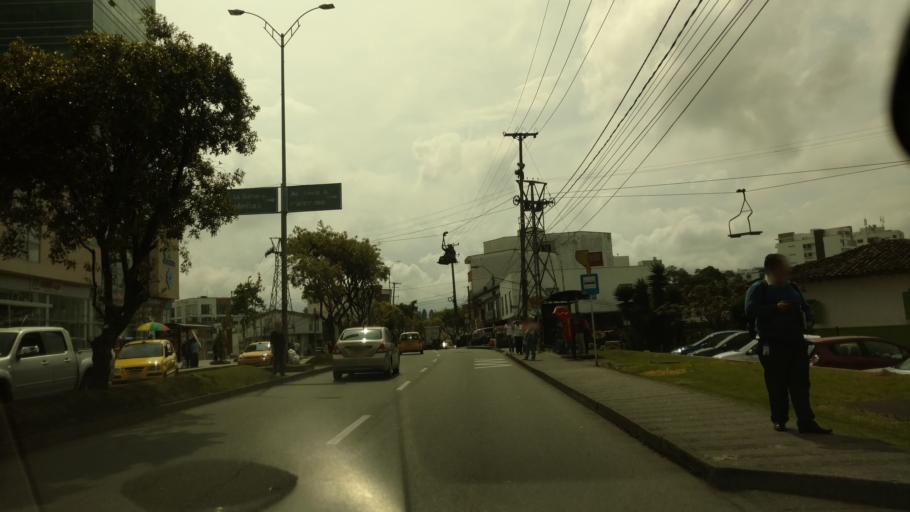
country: CO
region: Caldas
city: Villamaria
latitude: 5.0556
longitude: -75.4856
